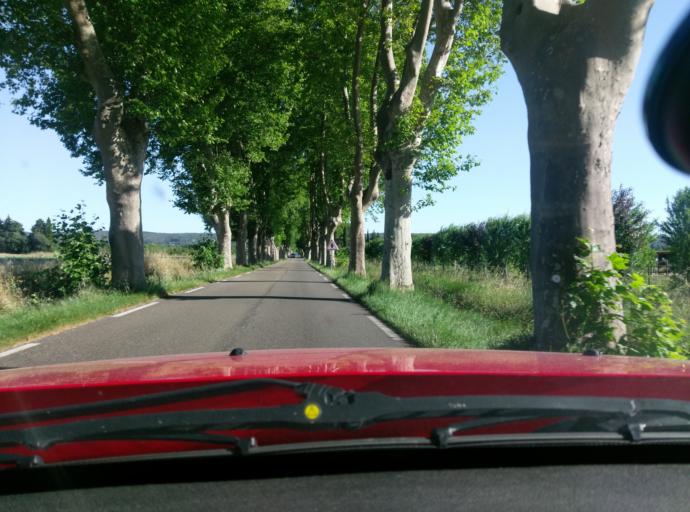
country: FR
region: Languedoc-Roussillon
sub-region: Departement du Gard
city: Uzes
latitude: 44.0391
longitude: 4.4080
